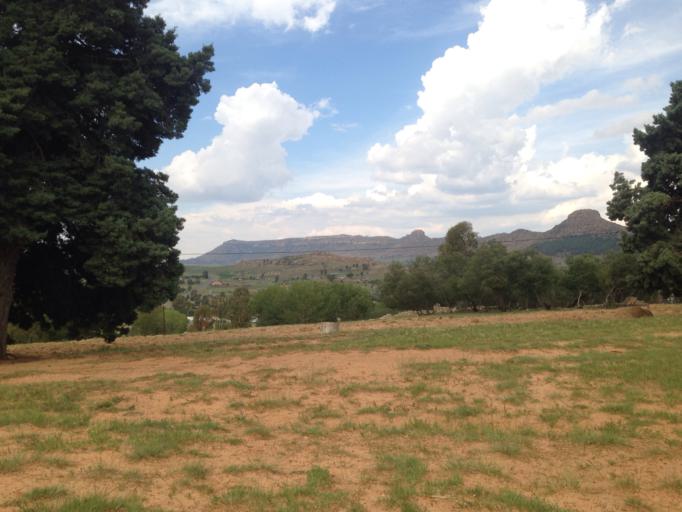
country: LS
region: Mafeteng
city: Mafeteng
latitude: -29.6944
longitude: 27.4327
